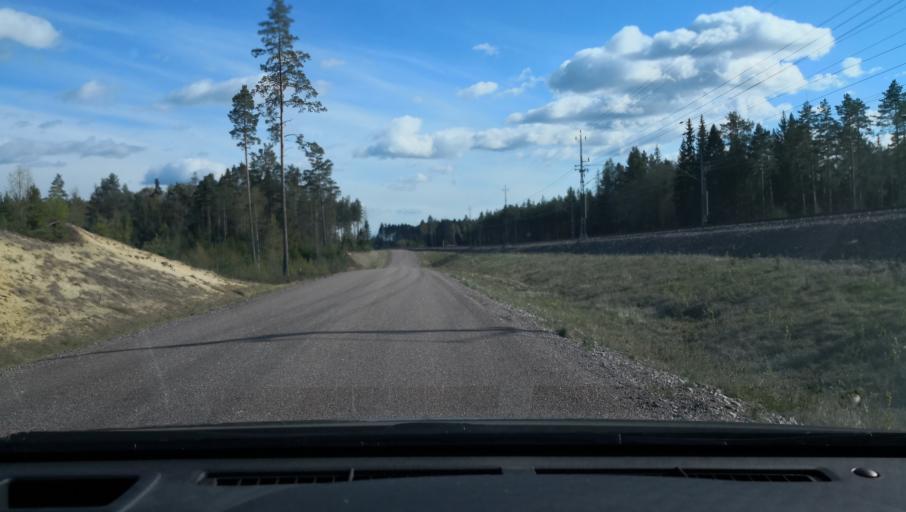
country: SE
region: OErebro
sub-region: Askersunds Kommun
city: Asbro
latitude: 58.9427
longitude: 15.0407
